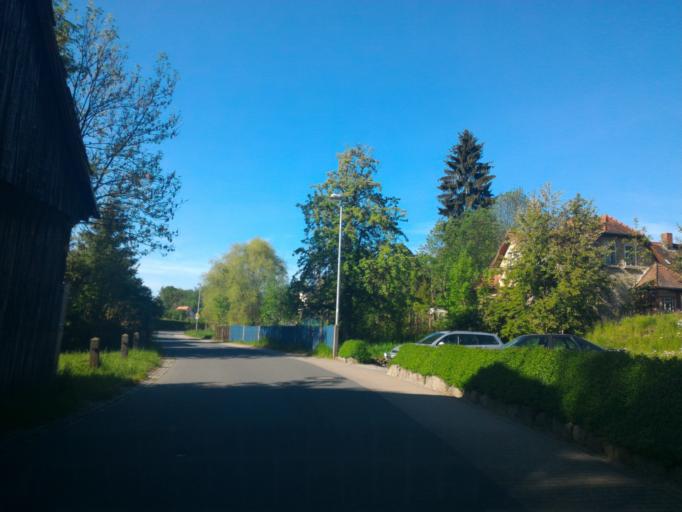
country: DE
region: Saxony
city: Grossschweidnitz
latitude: 51.0699
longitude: 14.6428
